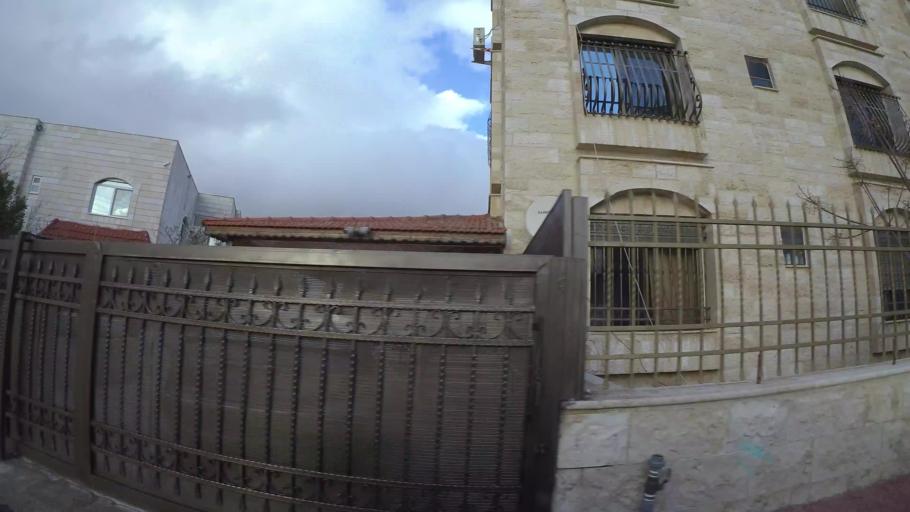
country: JO
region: Amman
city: Amman
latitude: 32.0038
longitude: 35.9240
